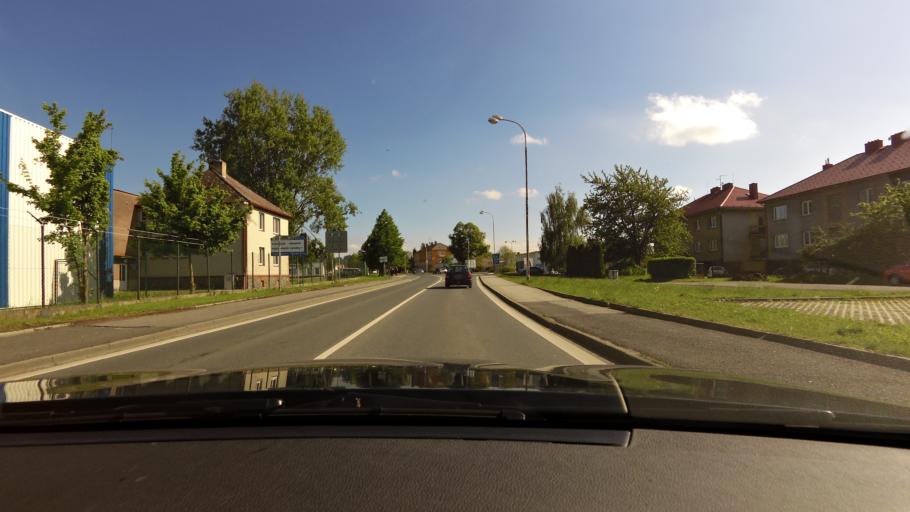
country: CZ
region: Plzensky
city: Klatovy
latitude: 49.3839
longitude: 13.2970
